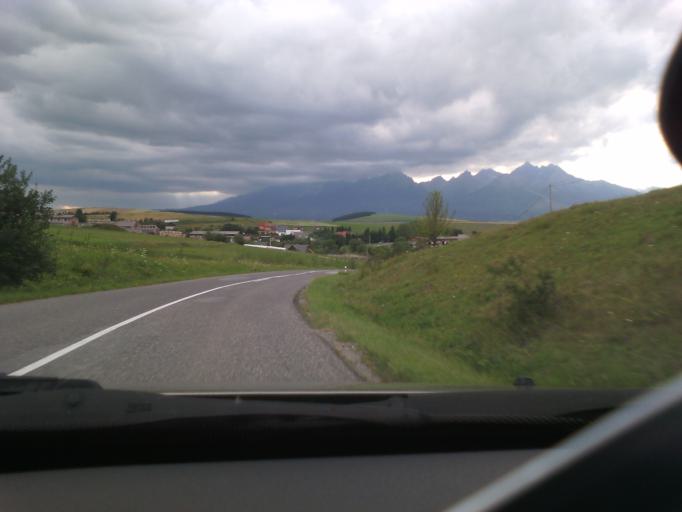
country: SK
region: Presovsky
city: Lubica
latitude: 49.0840
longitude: 20.4091
